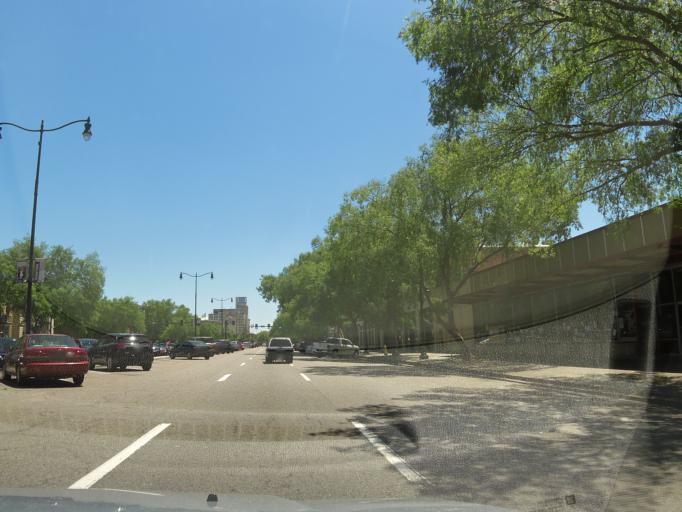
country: US
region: Georgia
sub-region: Richmond County
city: Augusta
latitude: 33.4775
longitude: -81.9723
